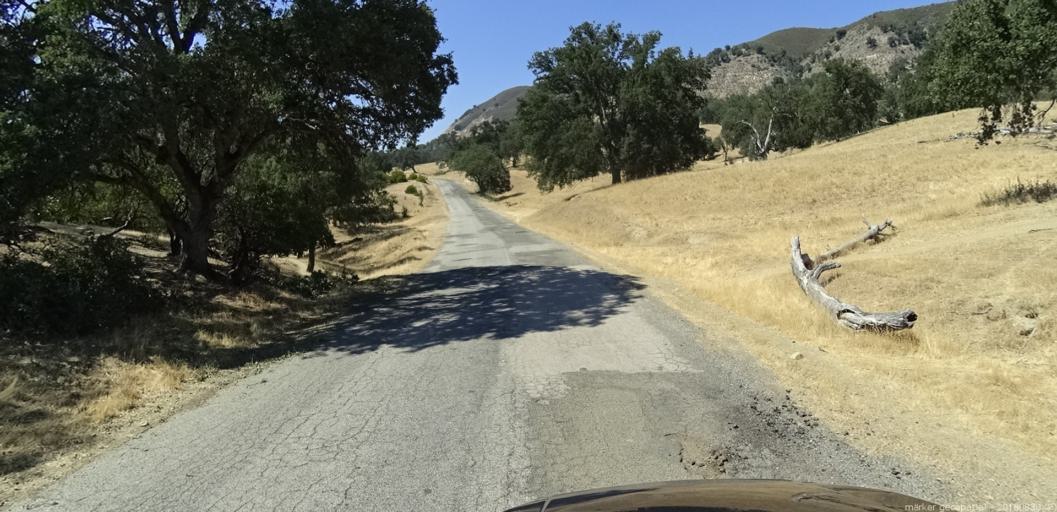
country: US
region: California
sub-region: Monterey County
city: Greenfield
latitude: 36.0861
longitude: -121.4033
